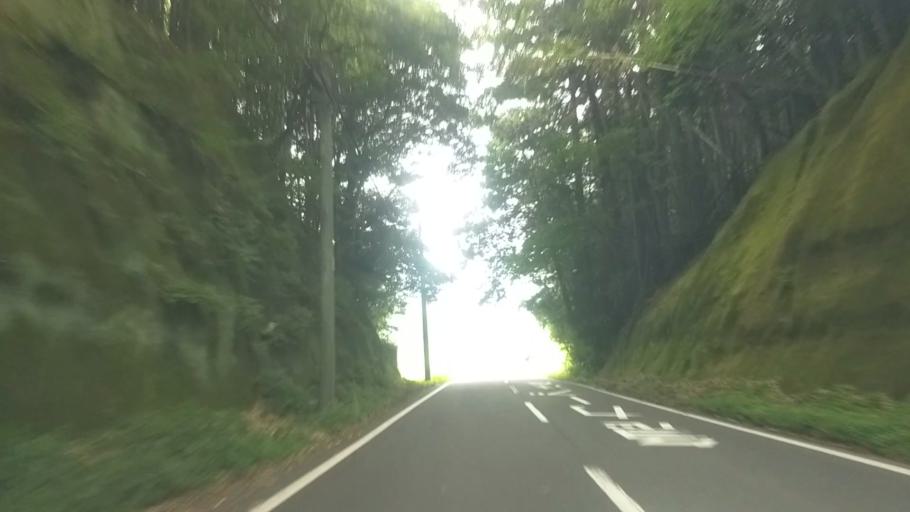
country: JP
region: Chiba
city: Kimitsu
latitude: 35.2422
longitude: 139.9960
